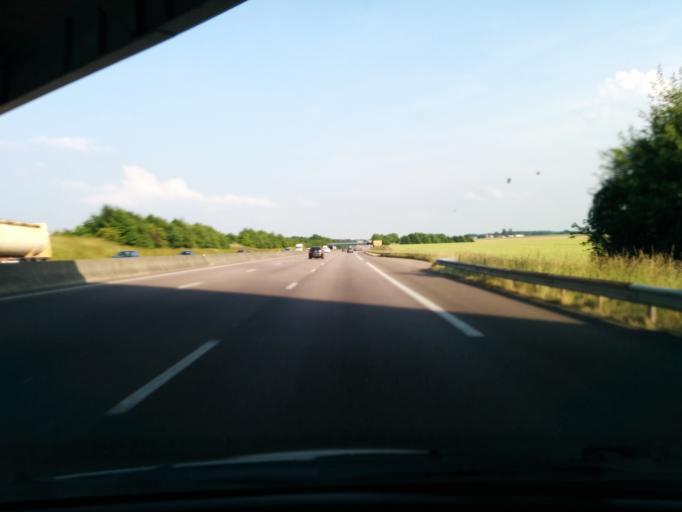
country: FR
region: Haute-Normandie
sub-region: Departement de l'Eure
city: La Chapelle-Reanville
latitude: 49.0937
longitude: 1.3641
